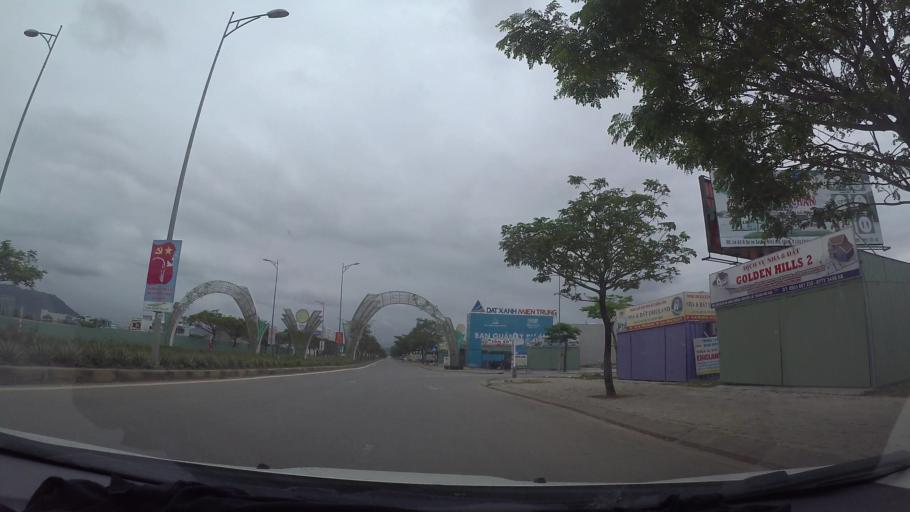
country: VN
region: Da Nang
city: Lien Chieu
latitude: 16.1046
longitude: 108.1226
